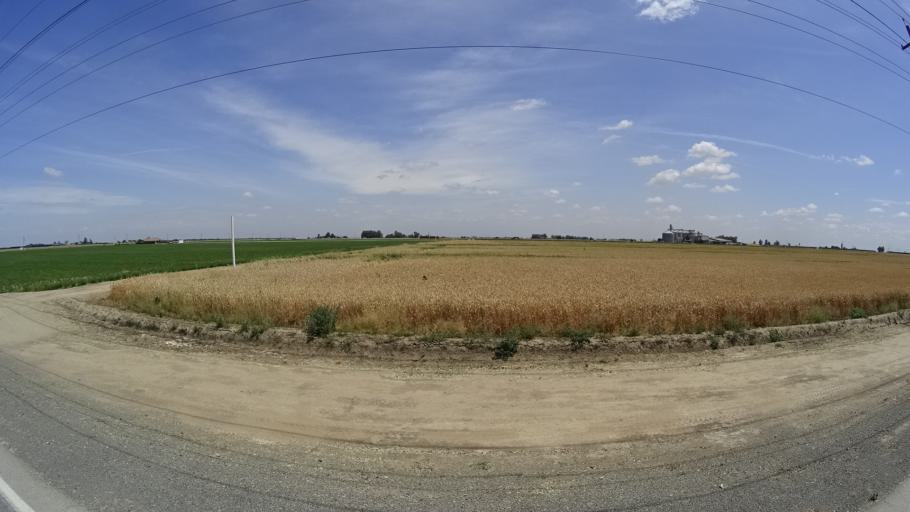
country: US
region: California
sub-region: Kings County
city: Home Garden
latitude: 36.2218
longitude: -119.6549
